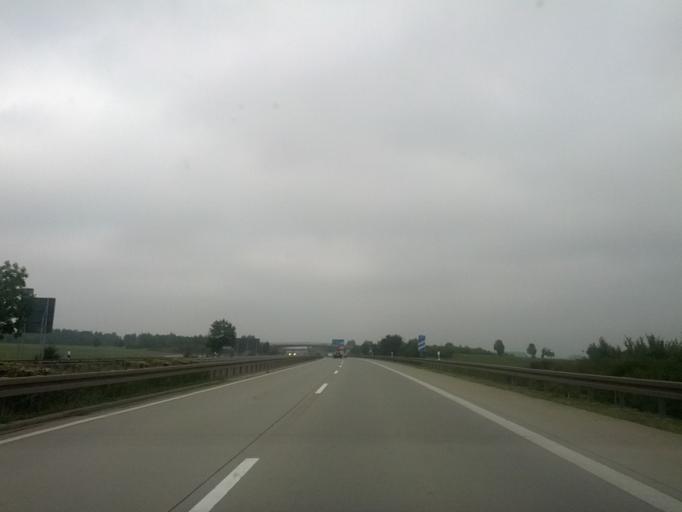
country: DE
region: Thuringia
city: Ingersleben
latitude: 50.9501
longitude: 10.9480
